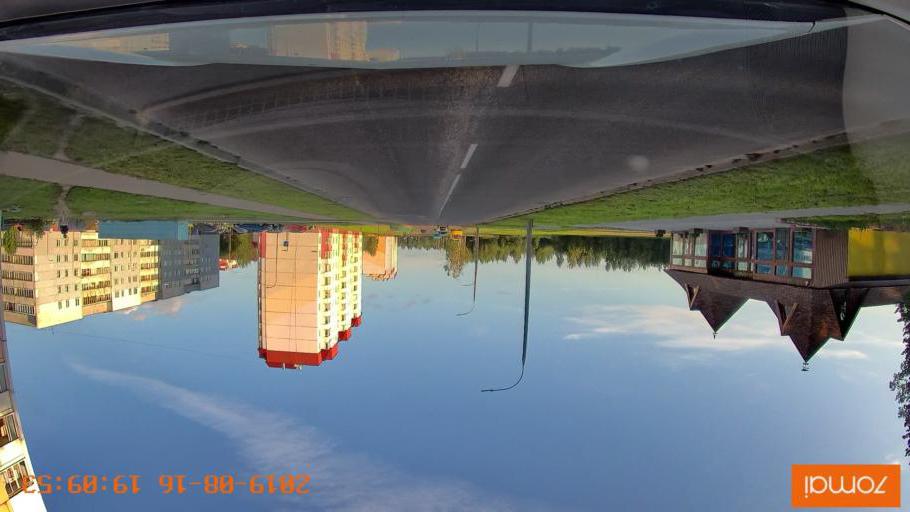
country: BY
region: Mogilev
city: Asipovichy
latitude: 53.3208
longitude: 28.6368
